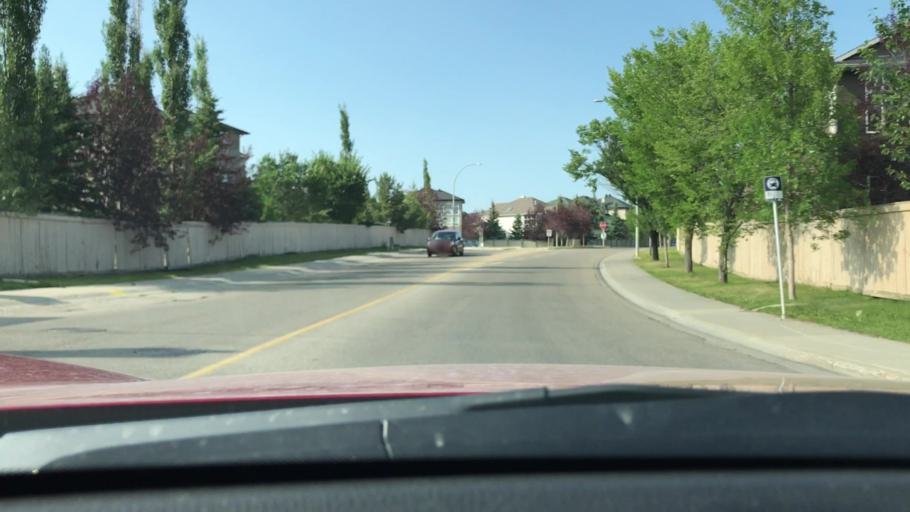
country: CA
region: Alberta
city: Calgary
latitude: 51.0294
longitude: -114.1823
